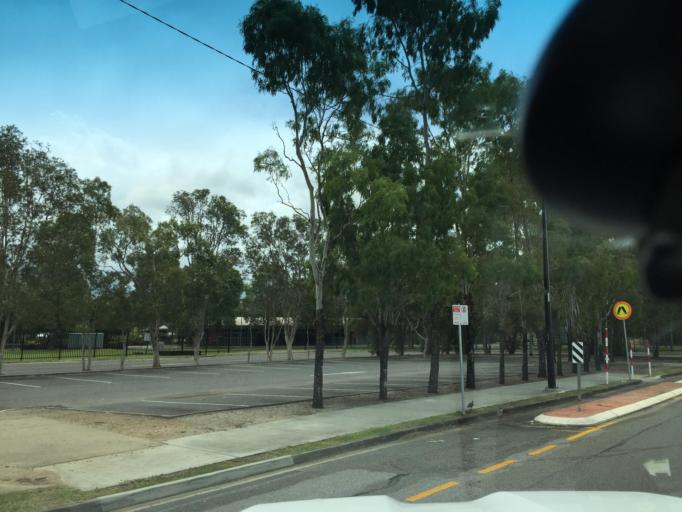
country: AU
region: Queensland
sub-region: Moreton Bay
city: Morayfield
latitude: -27.1109
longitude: 152.9248
